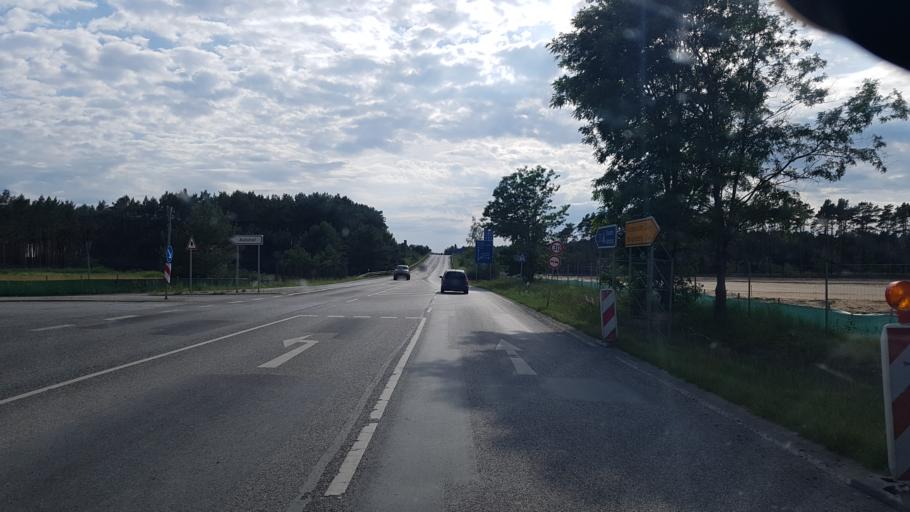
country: DE
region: Brandenburg
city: Grunheide
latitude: 52.3899
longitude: 13.7914
